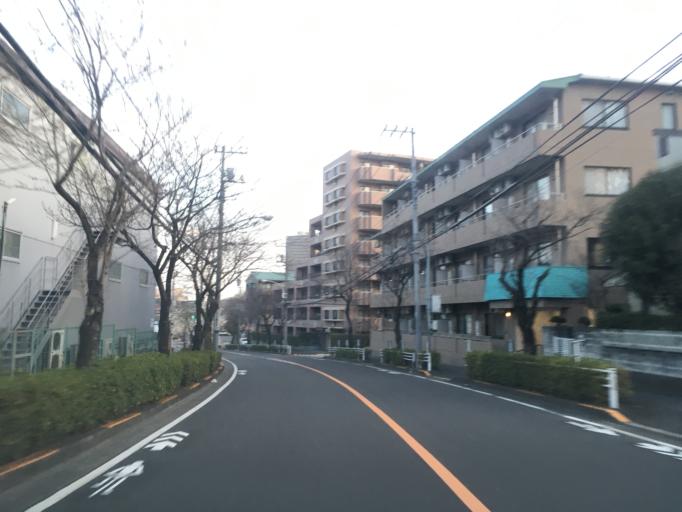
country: JP
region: Tokyo
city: Hino
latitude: 35.6091
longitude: 139.3860
